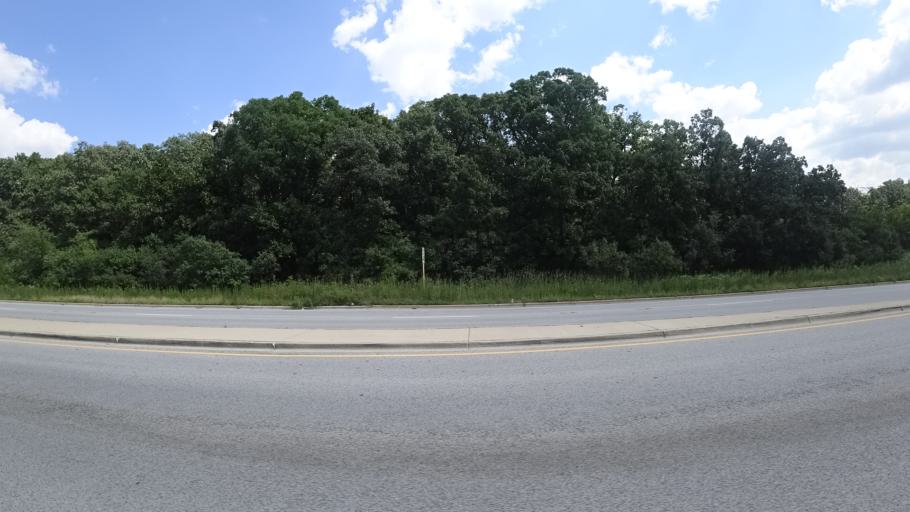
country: US
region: Illinois
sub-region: Cook County
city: Palos Heights
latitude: 41.6329
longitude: -87.7953
